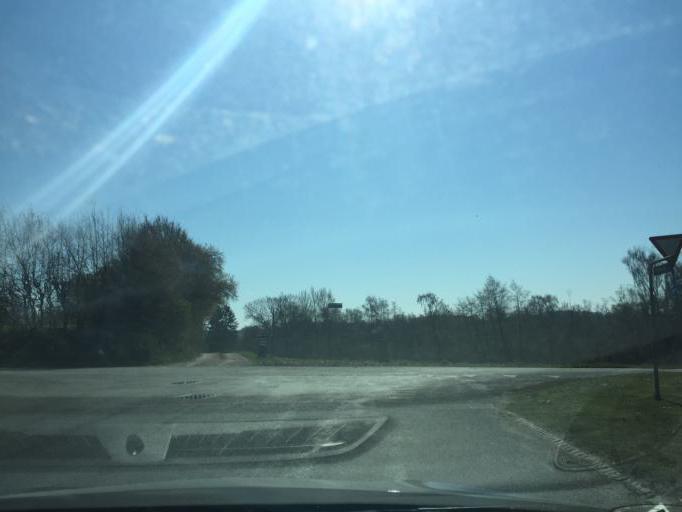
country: DK
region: South Denmark
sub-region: Faaborg-Midtfyn Kommune
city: Ringe
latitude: 55.2455
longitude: 10.4902
